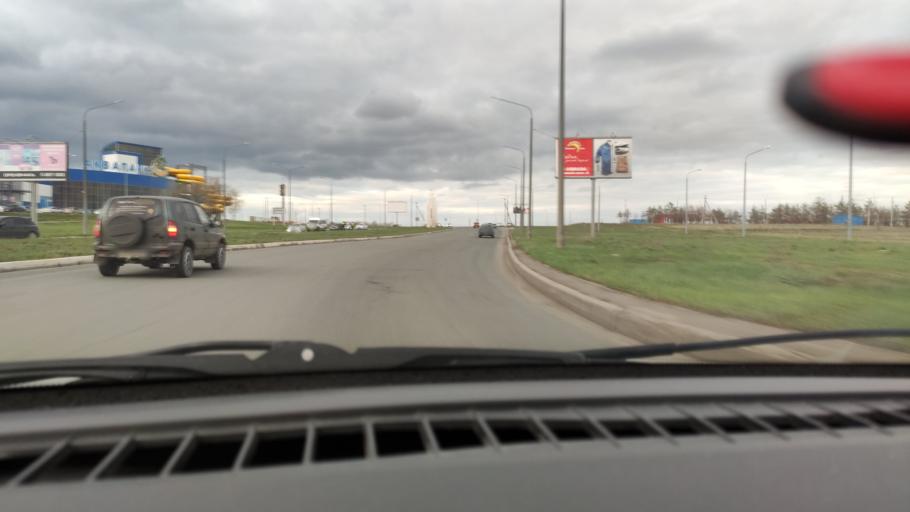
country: RU
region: Orenburg
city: Orenburg
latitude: 51.8103
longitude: 55.1807
